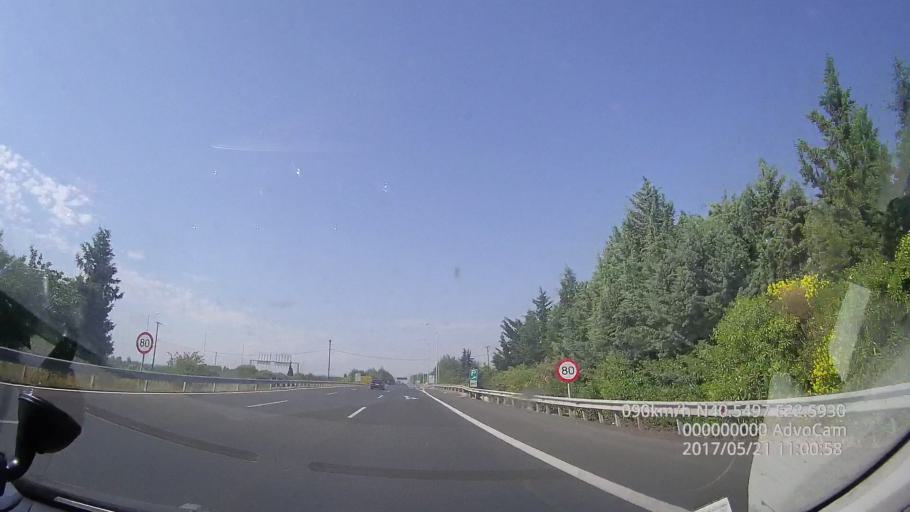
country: GR
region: Central Macedonia
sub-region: Nomos Imathias
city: Kleidi
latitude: 40.5494
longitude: 22.5928
